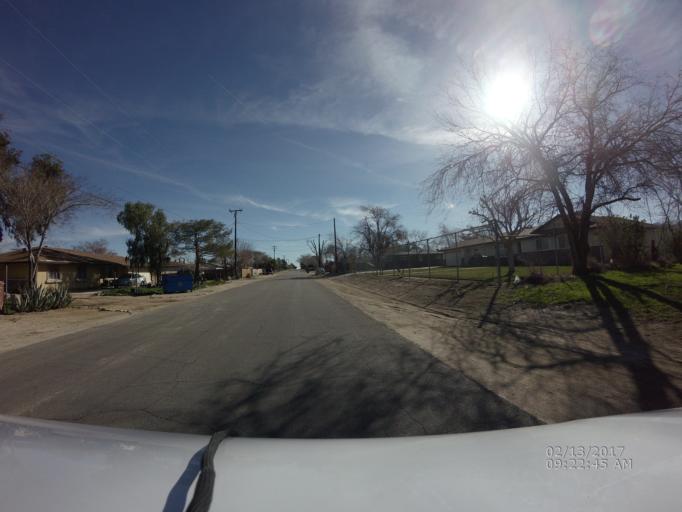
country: US
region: California
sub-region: Los Angeles County
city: Littlerock
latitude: 34.5302
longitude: -117.9696
